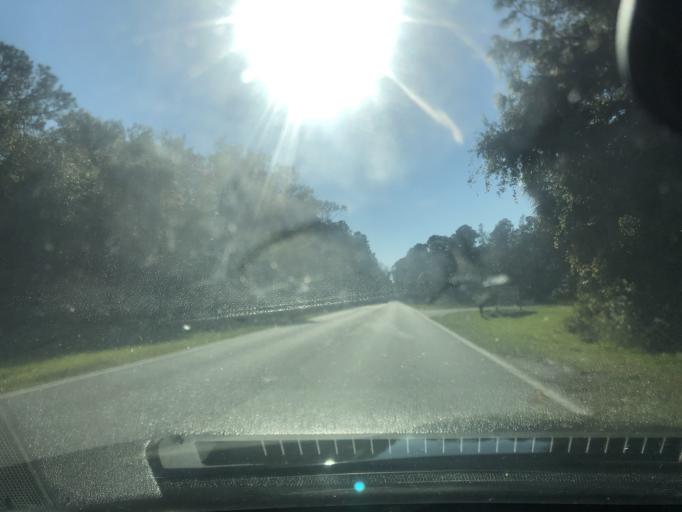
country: US
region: Florida
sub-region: Citrus County
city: Homosassa Springs
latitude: 28.8133
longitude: -82.5657
